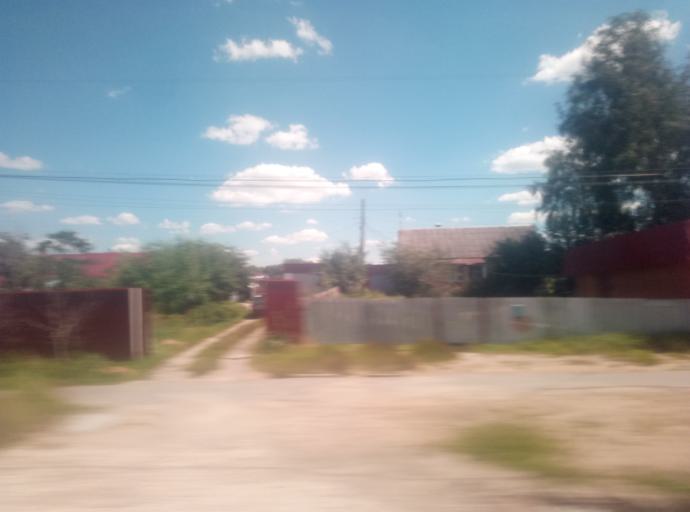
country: RU
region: Tula
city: Kireyevsk
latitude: 53.9844
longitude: 37.9330
